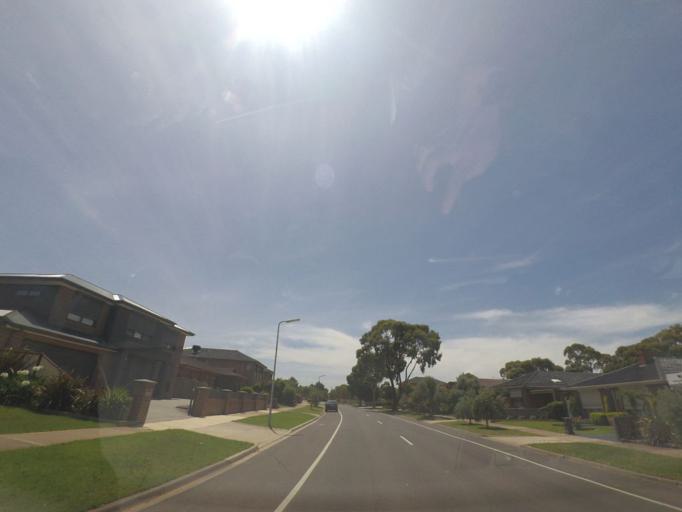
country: AU
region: Victoria
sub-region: Brimbank
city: Keilor Downs
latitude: -37.7204
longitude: 144.8034
